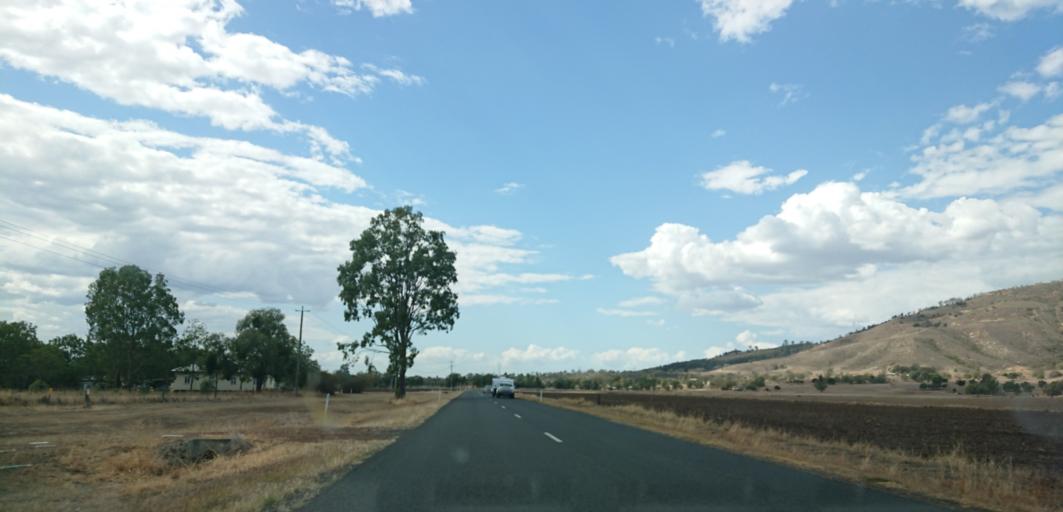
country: AU
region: Queensland
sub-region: Lockyer Valley
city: Gatton
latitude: -27.6500
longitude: 152.1743
